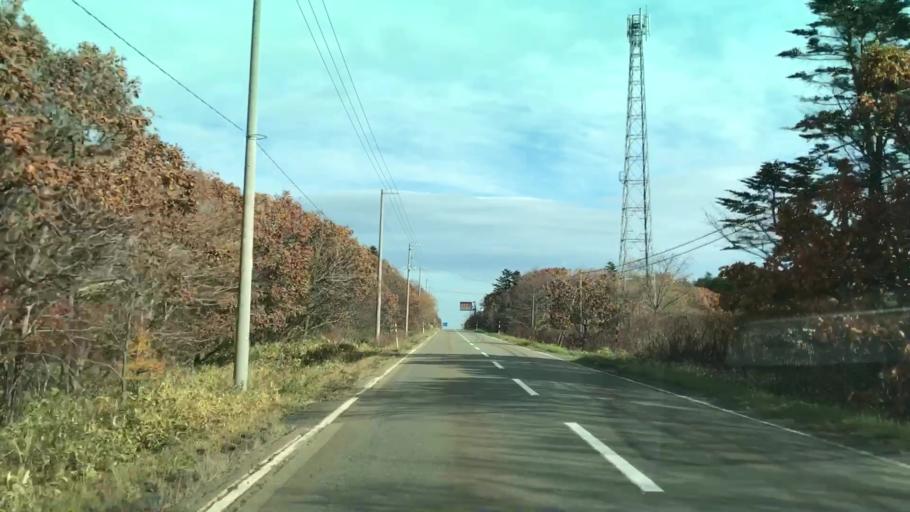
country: JP
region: Hokkaido
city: Obihiro
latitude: 42.0347
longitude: 143.2837
